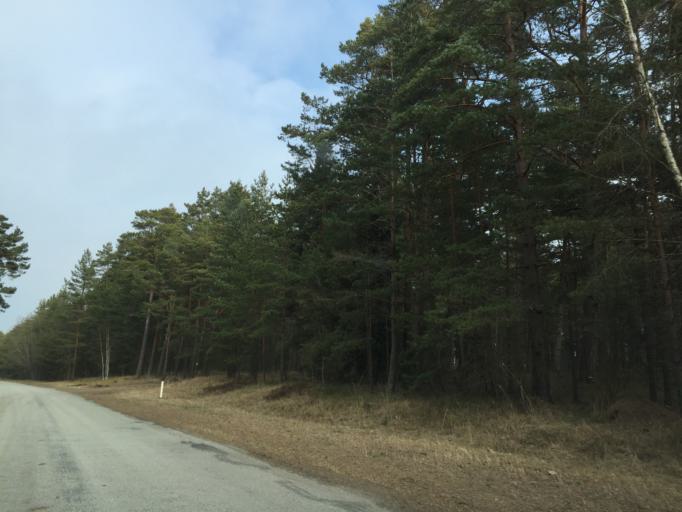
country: LV
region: Salacgrivas
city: Ainazi
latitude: 57.9308
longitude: 24.3918
